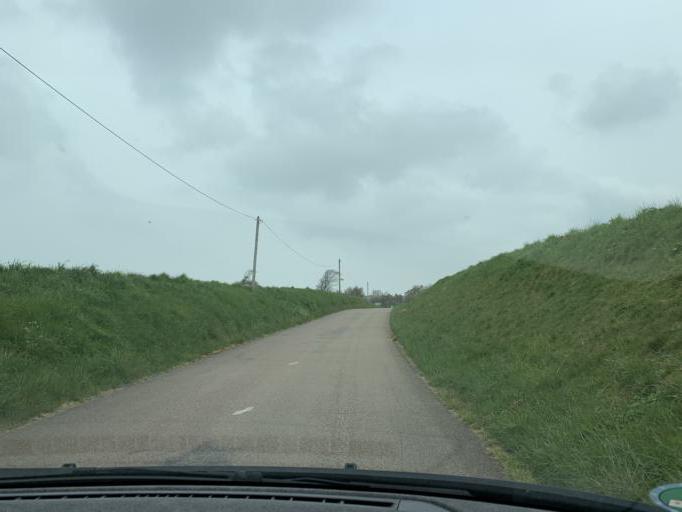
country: FR
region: Haute-Normandie
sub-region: Departement de la Seine-Maritime
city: Saint-Valery-en-Caux
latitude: 49.8537
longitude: 0.7838
